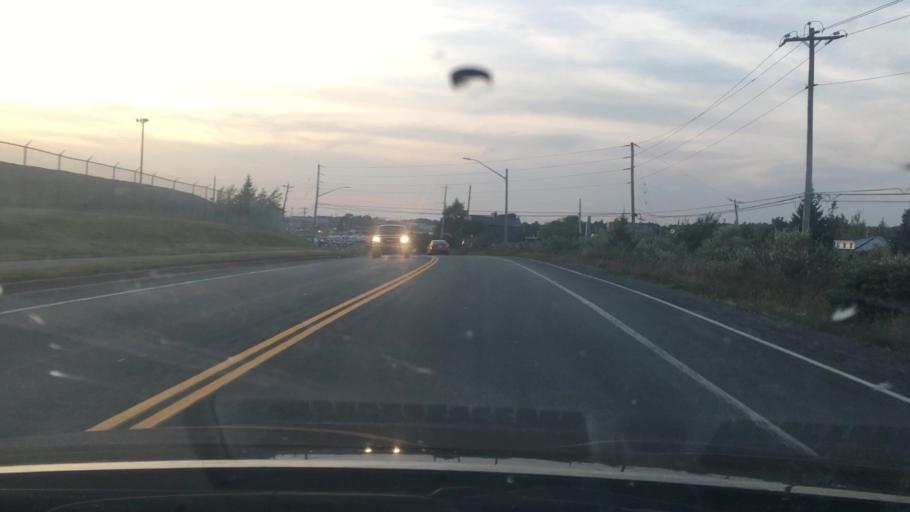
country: CA
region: Nova Scotia
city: Cole Harbour
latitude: 44.6191
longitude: -63.5031
